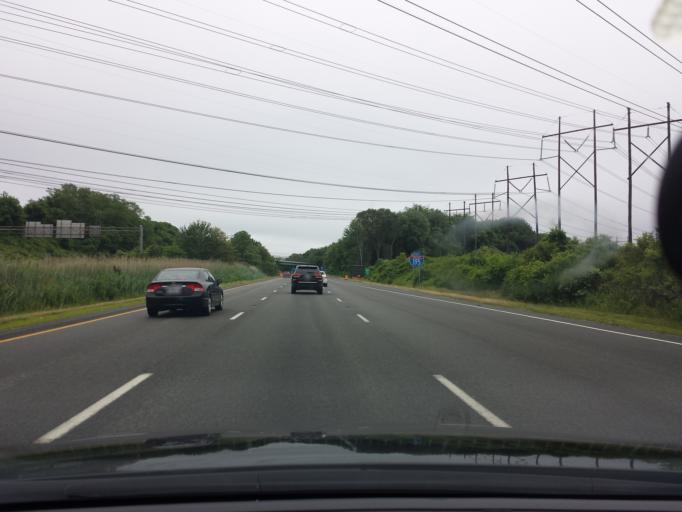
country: US
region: Massachusetts
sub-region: Bristol County
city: Ocean Grove
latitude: 41.7218
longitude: -71.1844
